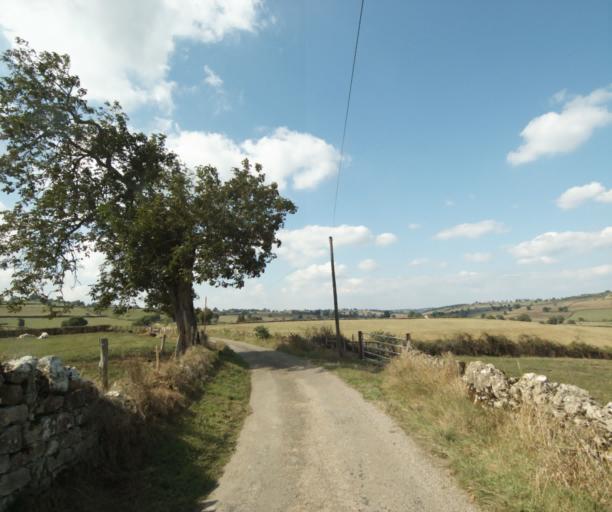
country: FR
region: Bourgogne
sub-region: Departement de Saone-et-Loire
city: Charolles
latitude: 46.3586
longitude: 4.2401
